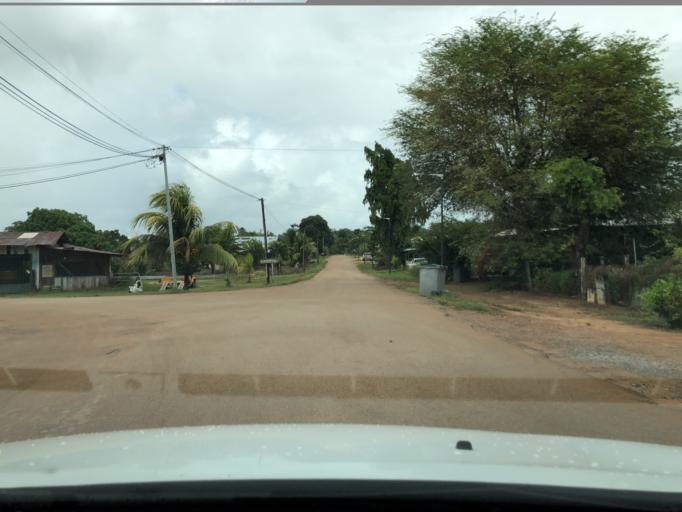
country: GF
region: Guyane
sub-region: Guyane
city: Mana
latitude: 5.6049
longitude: -53.8178
